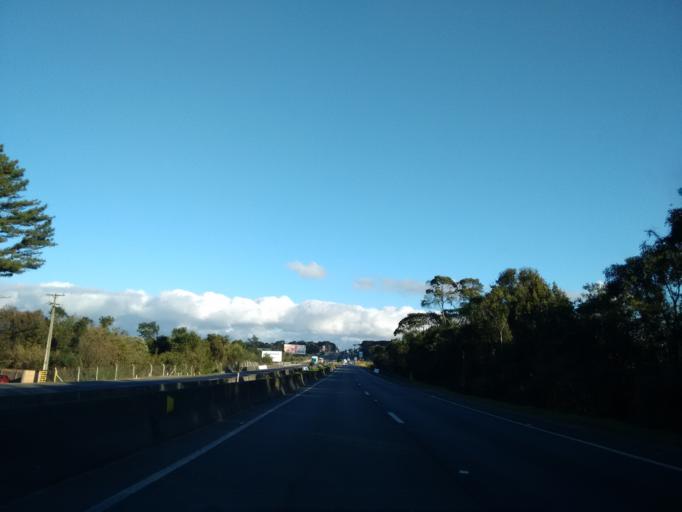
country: BR
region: Parana
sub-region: Sao Jose Dos Pinhais
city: Sao Jose dos Pinhais
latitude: -25.6368
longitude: -49.1609
